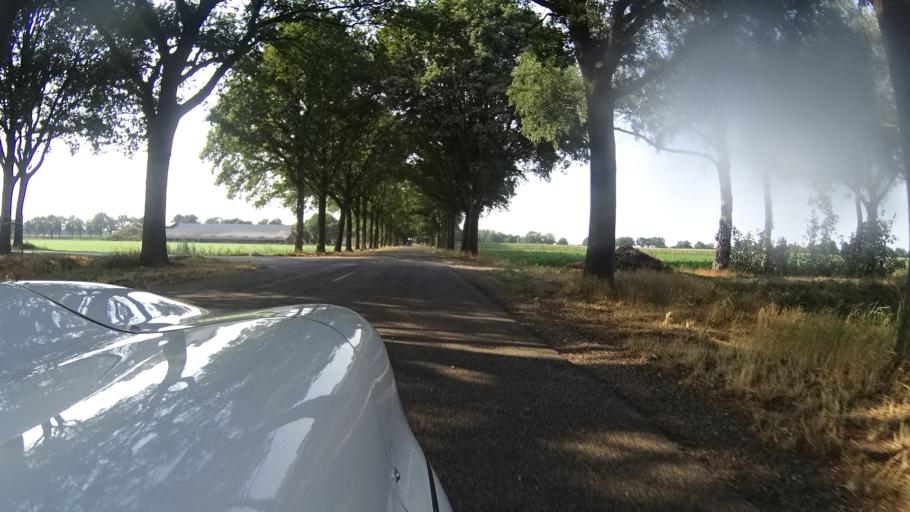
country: NL
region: North Brabant
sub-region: Gemeente Mill en Sint Hubert
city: Wilbertoord
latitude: 51.6404
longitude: 5.7826
